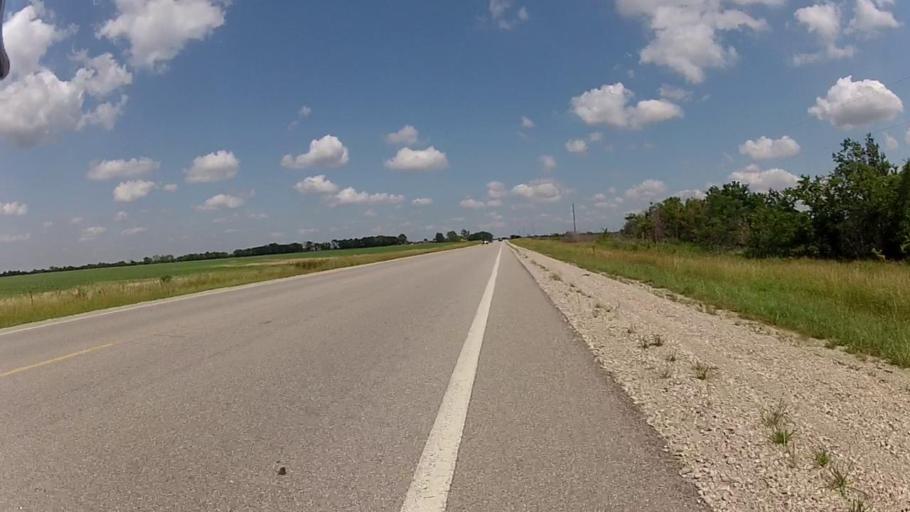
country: US
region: Kansas
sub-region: Labette County
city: Oswego
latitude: 37.1932
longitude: -95.1630
